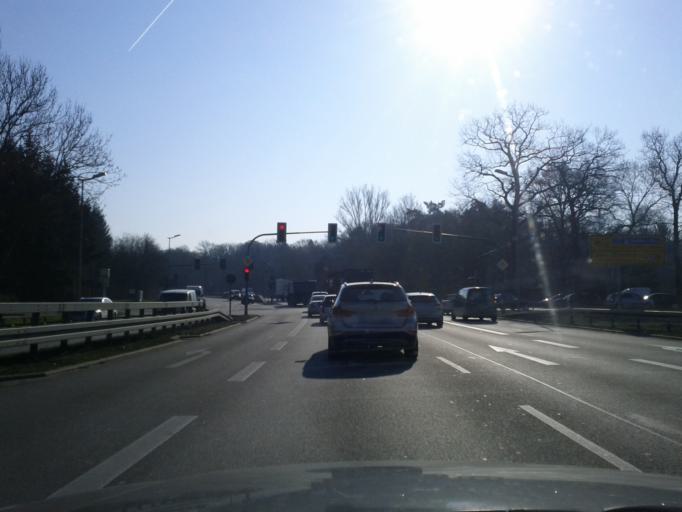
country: DE
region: Brandenburg
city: Hoppegarten
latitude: 52.4993
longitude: 13.6454
